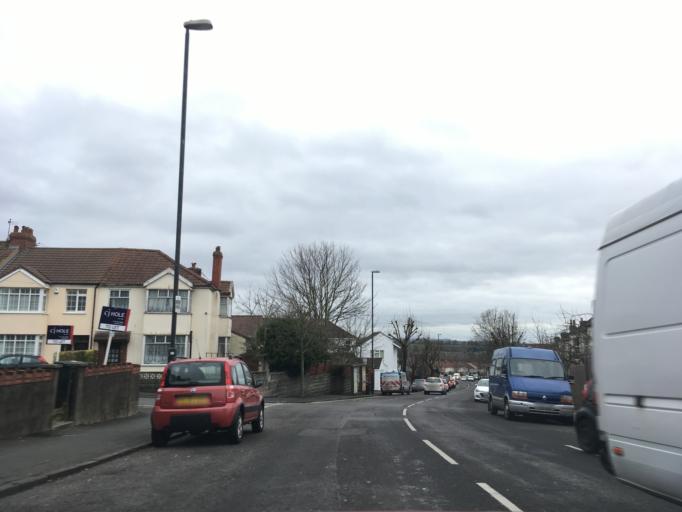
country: GB
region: England
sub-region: Bristol
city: Bristol
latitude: 51.4895
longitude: -2.5843
